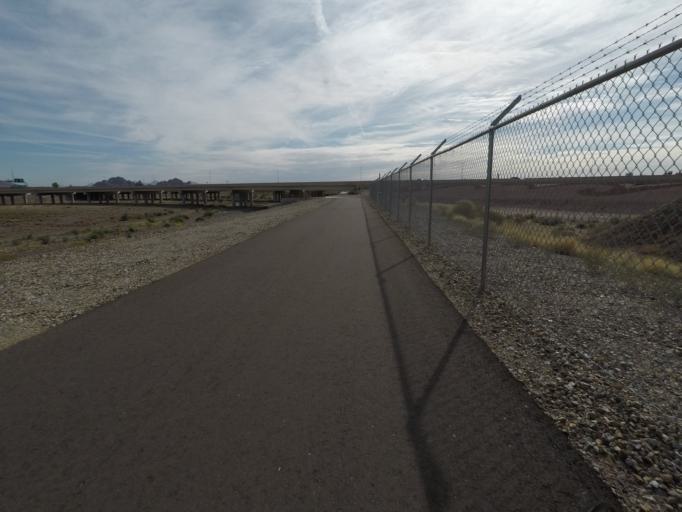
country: US
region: Arizona
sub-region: Maricopa County
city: Tempe Junction
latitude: 33.4300
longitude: -111.9813
